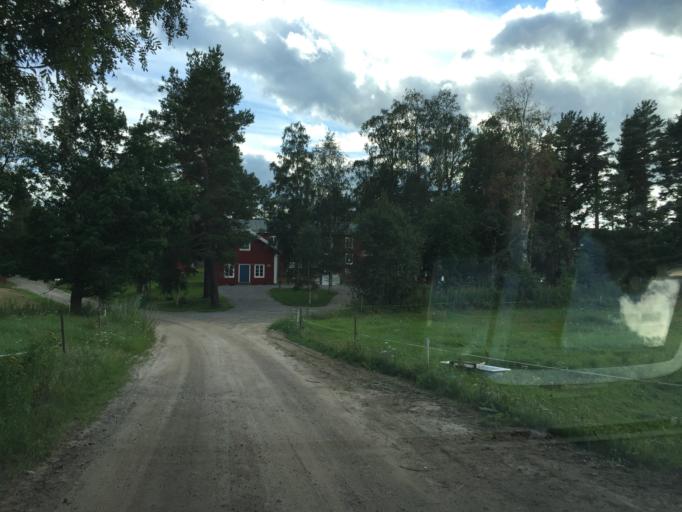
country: SE
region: Gaevleborg
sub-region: Ljusdals Kommun
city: Jaervsoe
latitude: 61.7537
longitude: 16.1704
